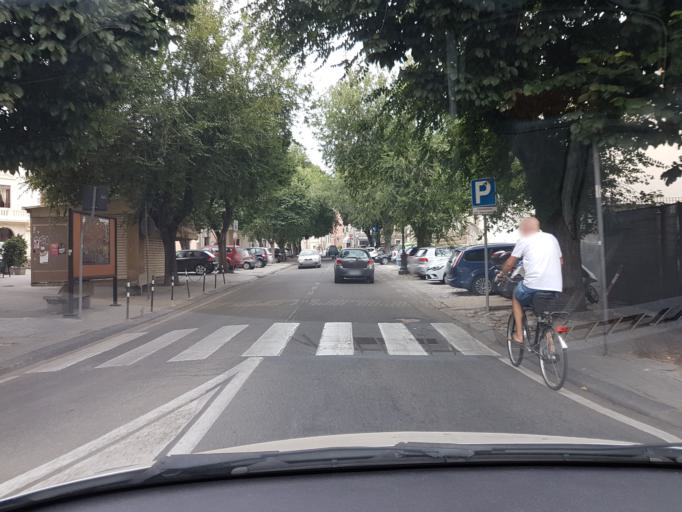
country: IT
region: Sardinia
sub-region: Provincia di Oristano
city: Oristano
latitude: 39.9008
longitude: 8.5918
